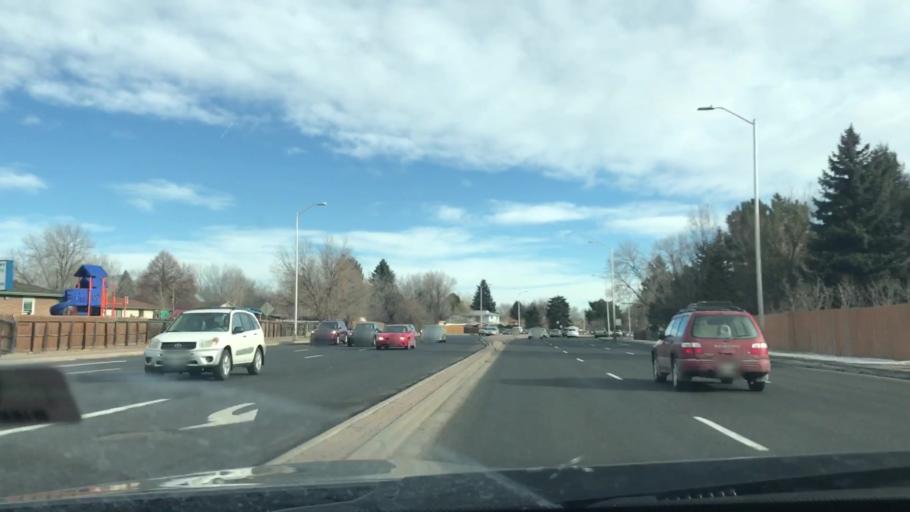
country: US
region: Colorado
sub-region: El Paso County
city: Cimarron Hills
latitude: 38.9007
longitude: -104.7662
